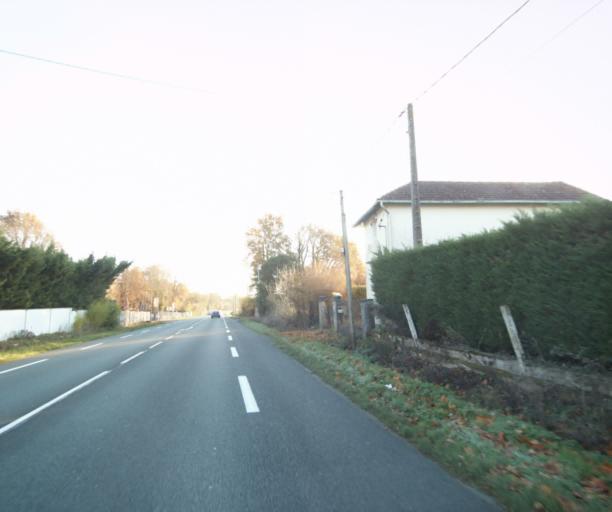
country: FR
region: Poitou-Charentes
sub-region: Departement de la Charente-Maritime
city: Fontcouverte
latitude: 45.7454
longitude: -0.5842
